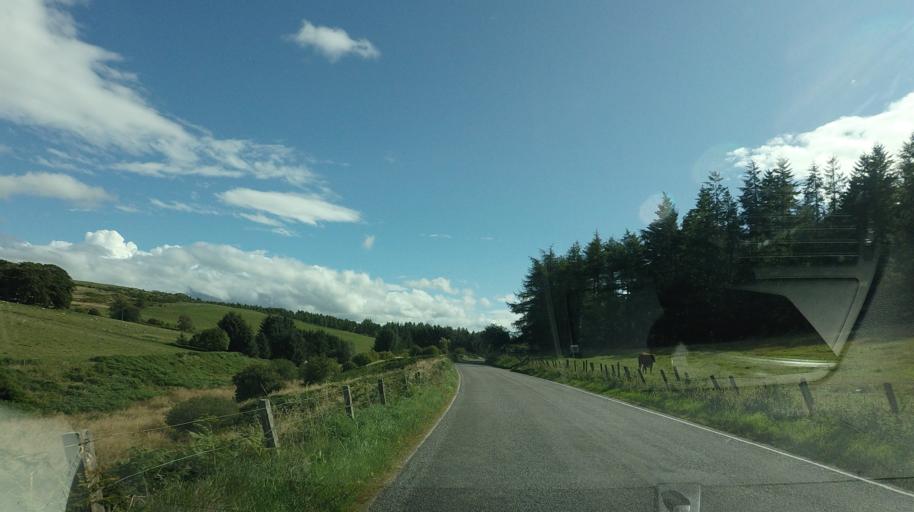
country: GB
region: Scotland
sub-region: Aberdeenshire
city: Torphins
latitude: 57.1353
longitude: -2.7029
